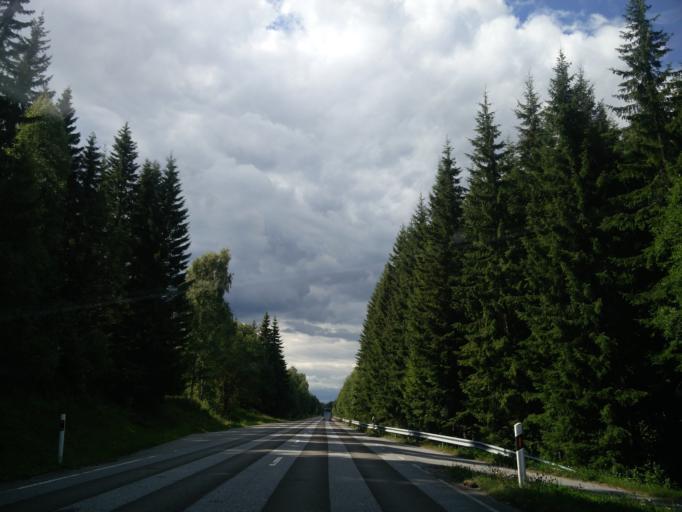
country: SE
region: OErebro
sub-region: Hallefors Kommun
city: Haellefors
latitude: 59.7590
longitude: 14.4314
